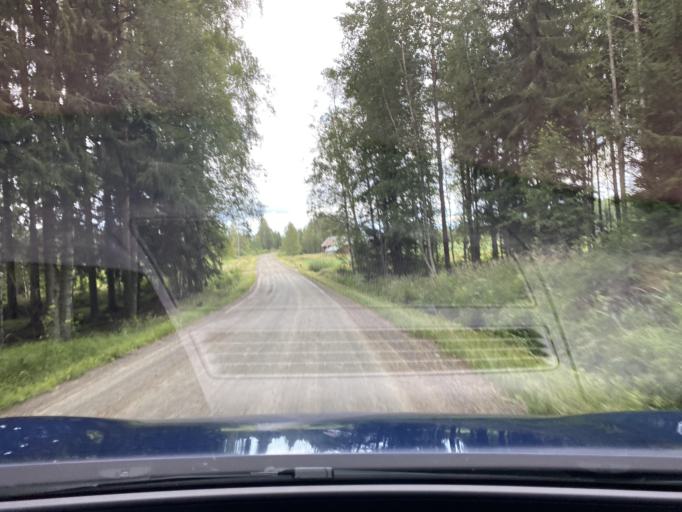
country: FI
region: Pirkanmaa
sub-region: Lounais-Pirkanmaa
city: Punkalaidun
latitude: 61.2178
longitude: 23.1664
